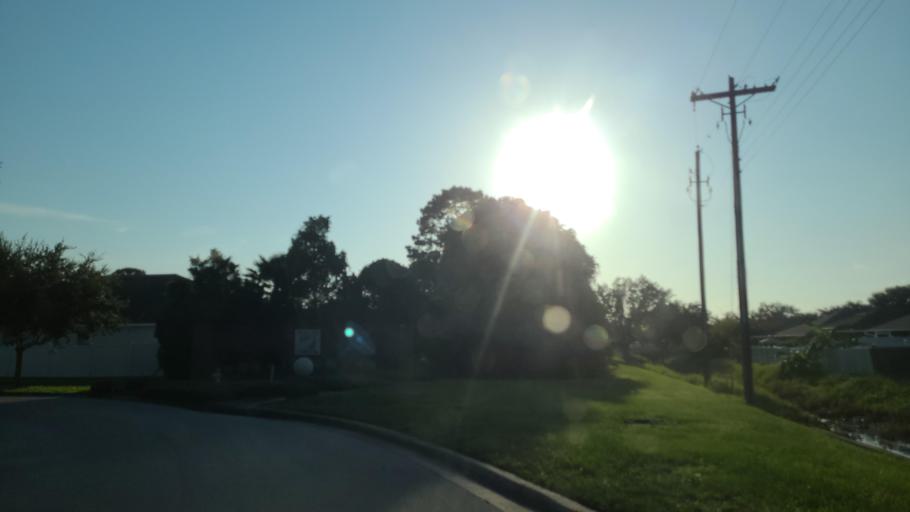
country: US
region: Florida
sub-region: Hillsborough County
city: Riverview
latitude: 27.8104
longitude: -82.3361
